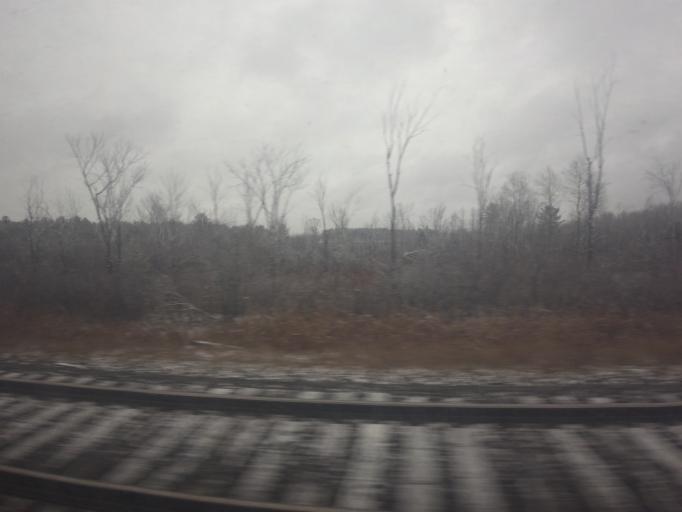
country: US
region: New York
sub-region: Jefferson County
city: Alexandria Bay
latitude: 44.4306
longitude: -75.9724
